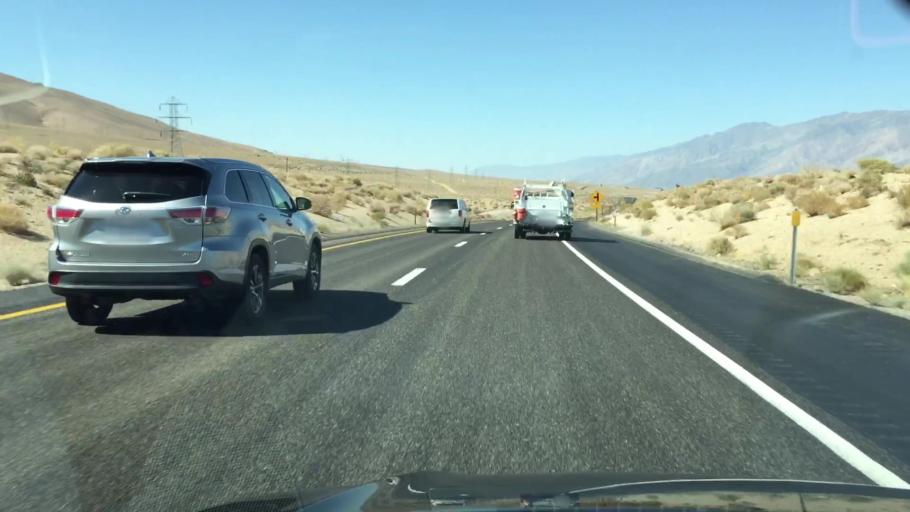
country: US
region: California
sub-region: Inyo County
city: Lone Pine
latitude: 36.4410
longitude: -118.0342
